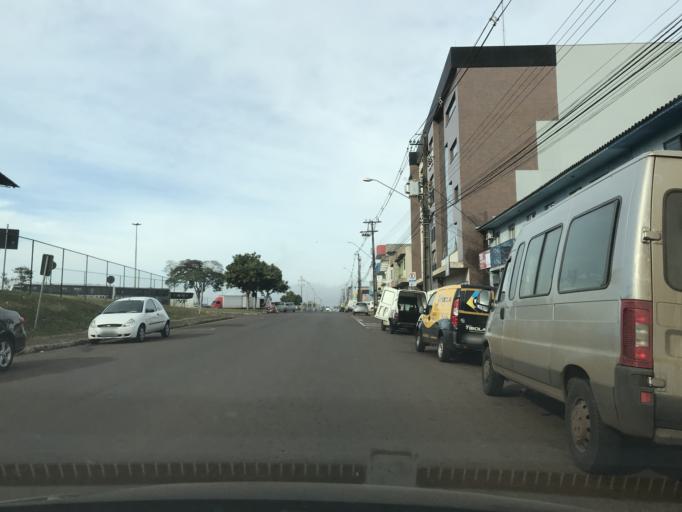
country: BR
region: Parana
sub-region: Cascavel
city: Cascavel
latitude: -24.9575
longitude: -53.4807
